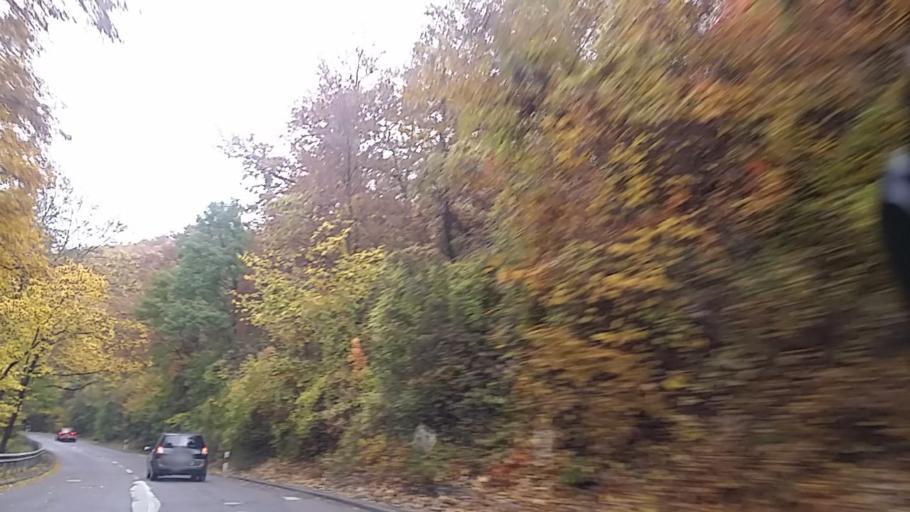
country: HU
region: Heves
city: Felsotarkany
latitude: 47.9659
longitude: 20.3492
